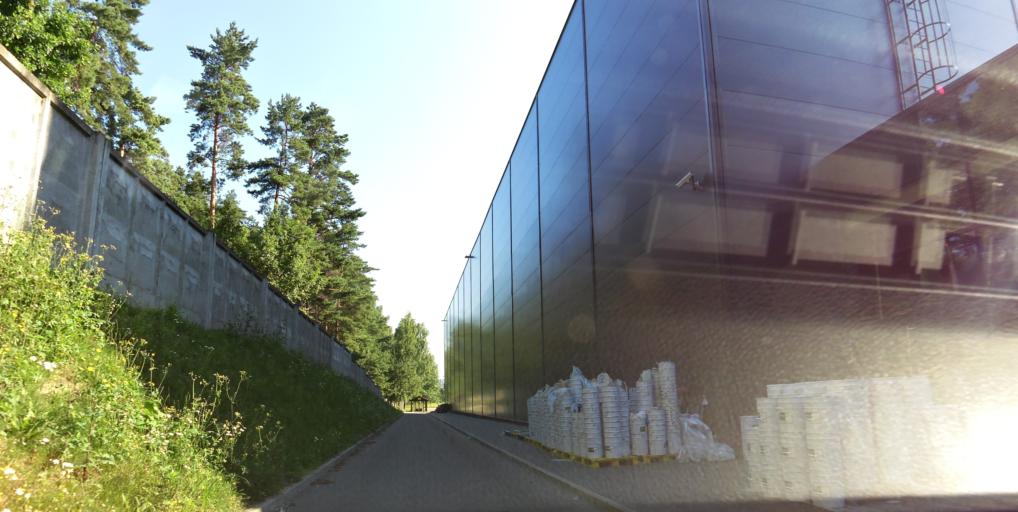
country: LT
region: Vilnius County
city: Seskine
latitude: 54.7082
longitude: 25.2334
